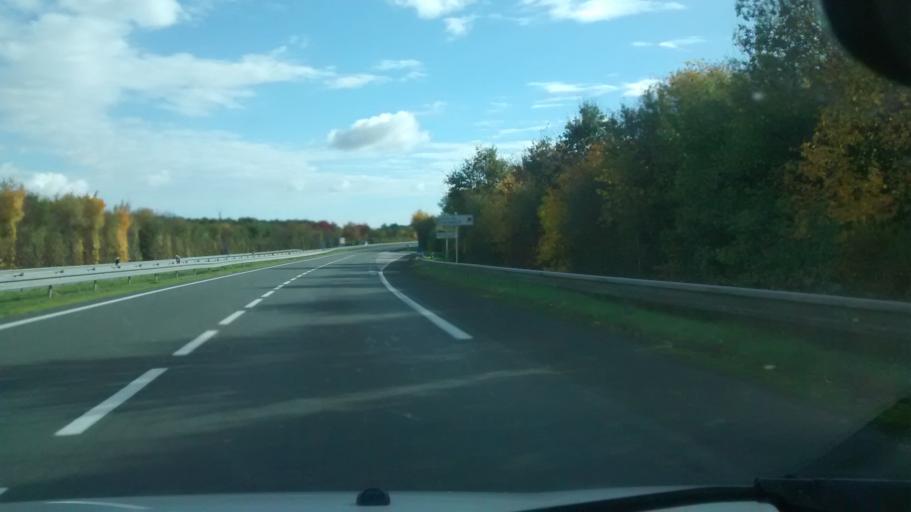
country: FR
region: Pays de la Loire
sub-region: Departement de Maine-et-Loire
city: Pouance
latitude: 47.7600
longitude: -1.1951
